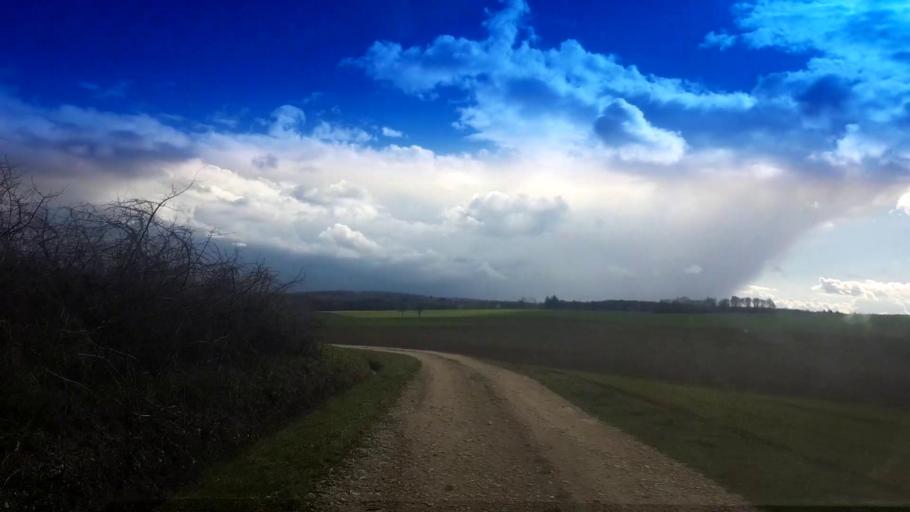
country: DE
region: Bavaria
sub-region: Upper Franconia
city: Schesslitz
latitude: 49.9974
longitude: 11.0136
